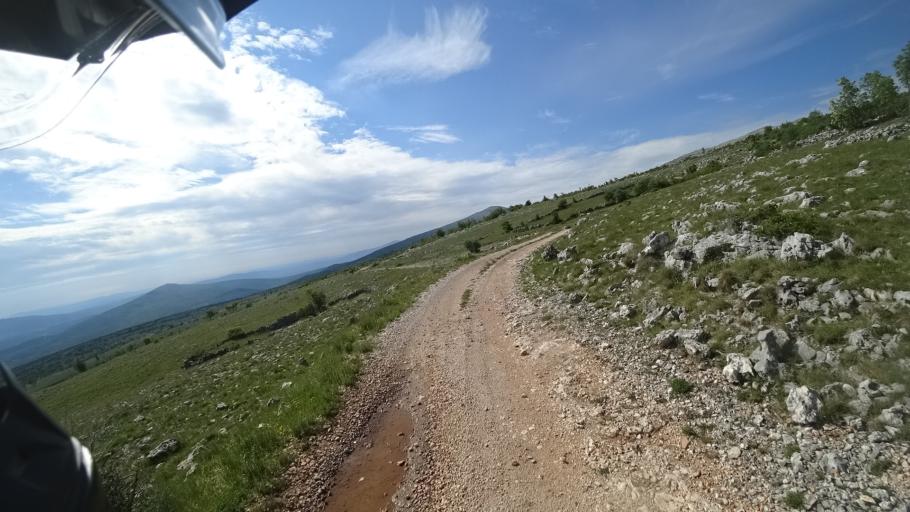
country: HR
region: Splitsko-Dalmatinska
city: Hrvace
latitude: 43.7744
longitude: 16.4573
